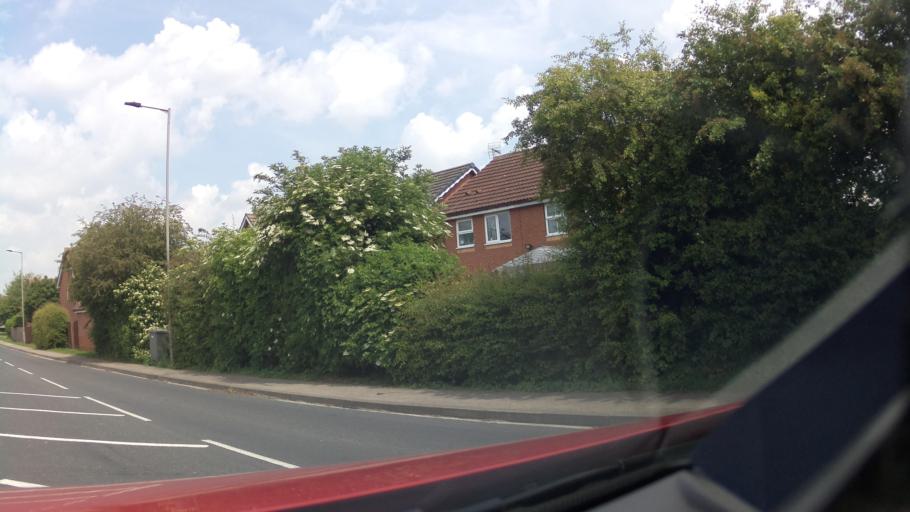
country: GB
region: England
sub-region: North Yorkshire
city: Boroughbridge
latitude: 54.0852
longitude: -1.3960
